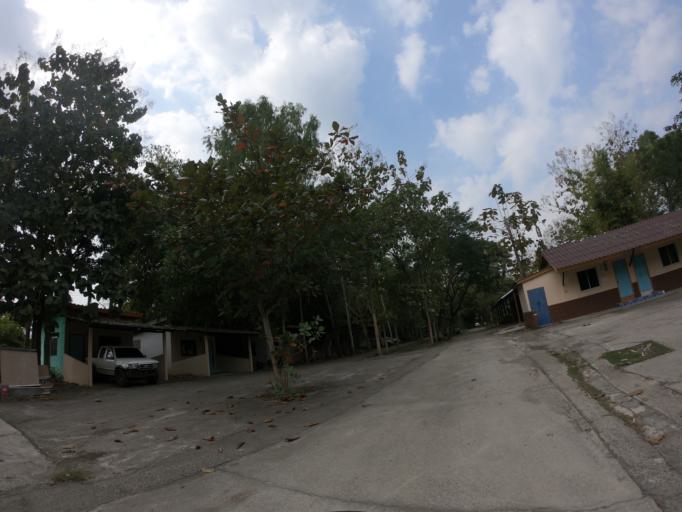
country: TH
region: Chiang Mai
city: Chiang Mai
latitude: 18.7640
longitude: 98.9712
